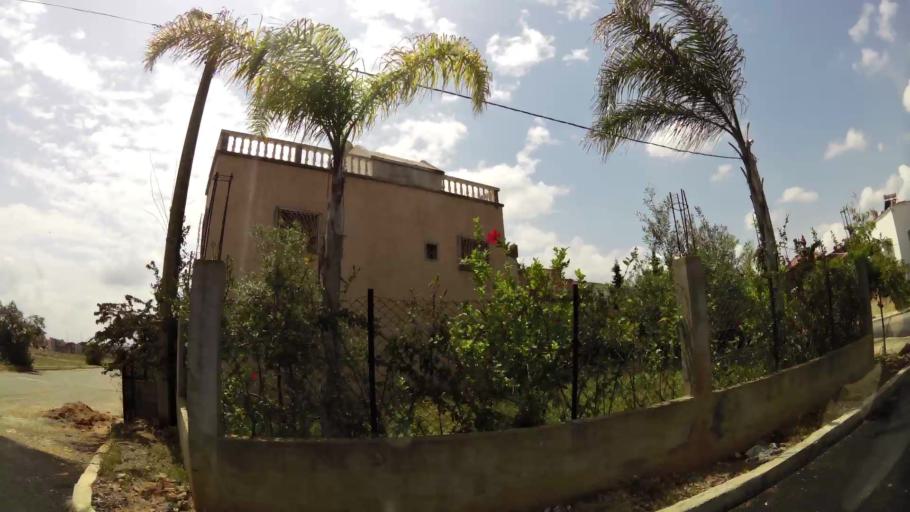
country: MA
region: Gharb-Chrarda-Beni Hssen
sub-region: Kenitra Province
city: Kenitra
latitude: 34.0146
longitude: -6.5319
